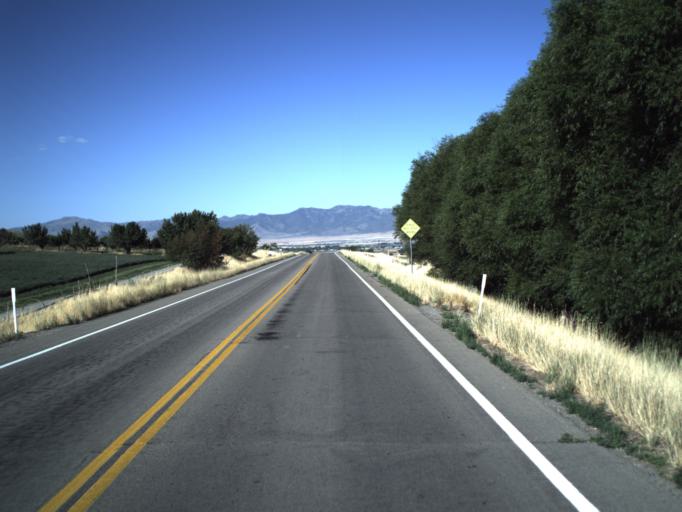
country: US
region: Utah
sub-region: Utah County
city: Genola
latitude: 39.9788
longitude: -111.8377
